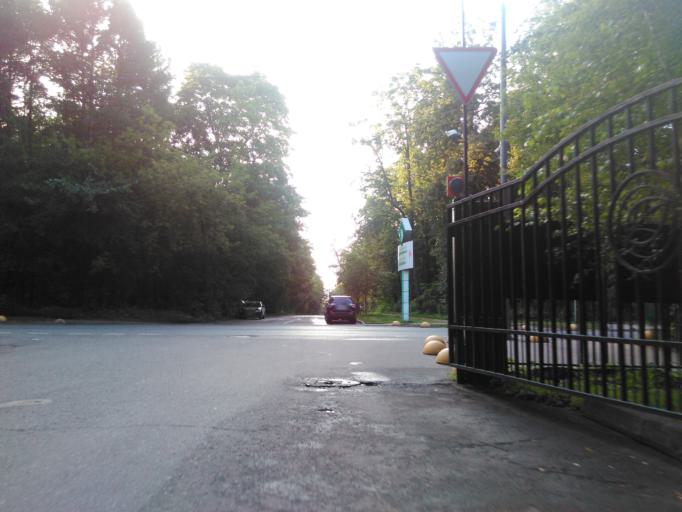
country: RU
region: Moscow
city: Sokol'niki
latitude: 55.8046
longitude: 37.6633
